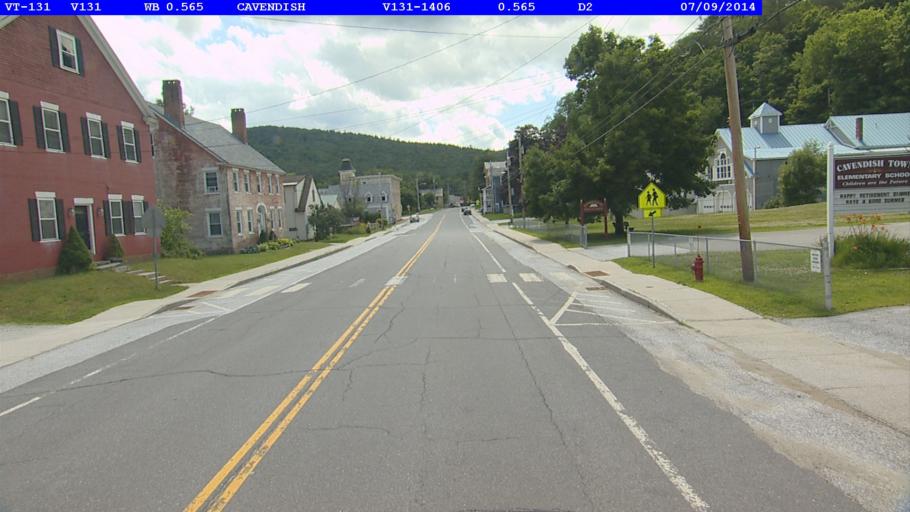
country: US
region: Vermont
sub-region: Windsor County
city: Chester
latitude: 43.3836
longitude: -72.6370
